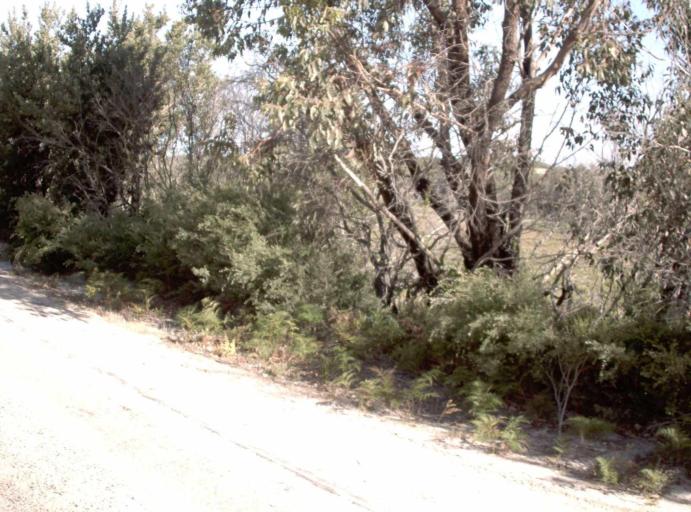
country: AU
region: Victoria
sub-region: East Gippsland
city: Lakes Entrance
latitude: -37.7975
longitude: 148.7039
